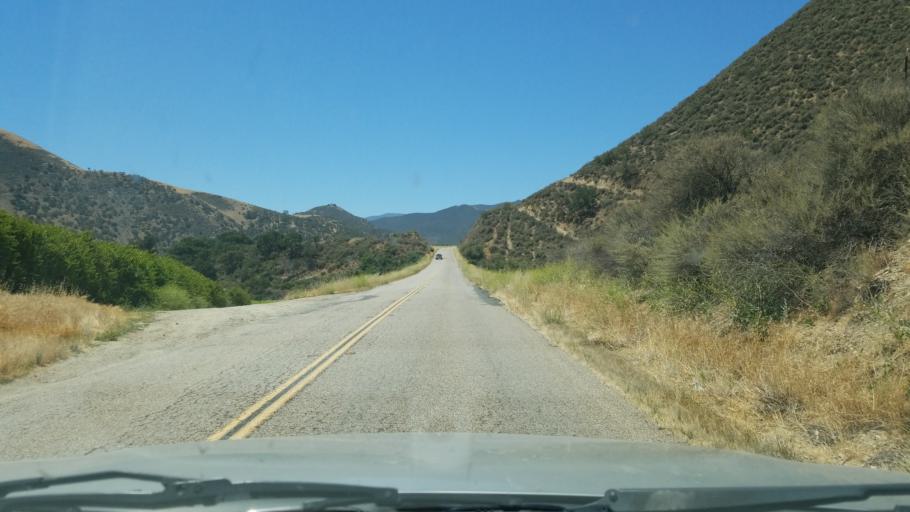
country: US
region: California
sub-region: Monterey County
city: Greenfield
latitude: 36.2747
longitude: -121.3334
